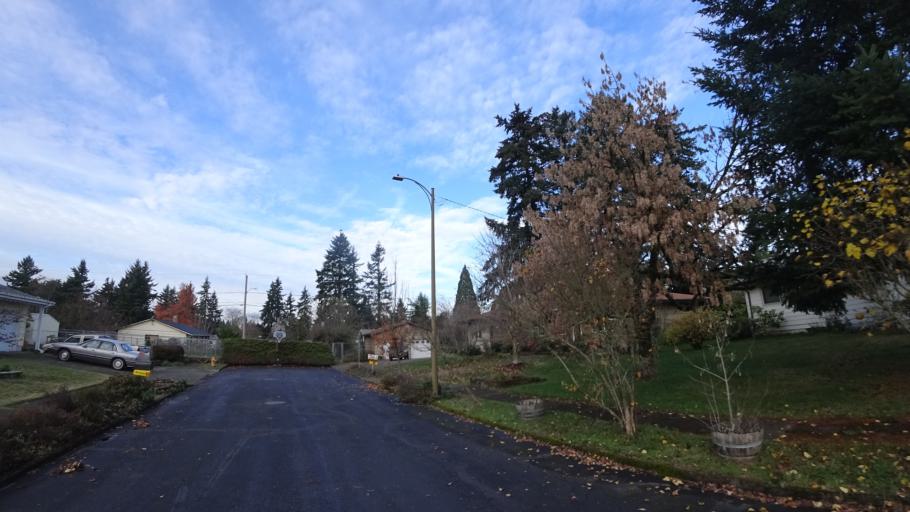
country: US
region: Oregon
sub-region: Multnomah County
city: Lents
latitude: 45.5167
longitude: -122.5279
